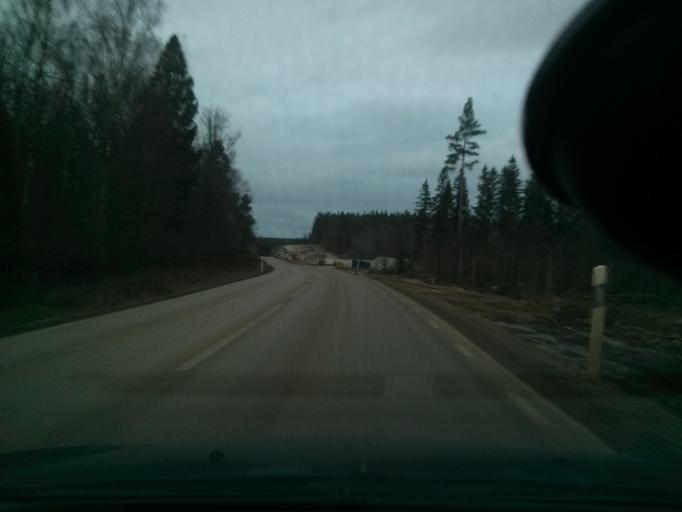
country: SE
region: Blekinge
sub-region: Ronneby Kommun
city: Brakne-Hoby
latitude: 56.3270
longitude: 15.1741
